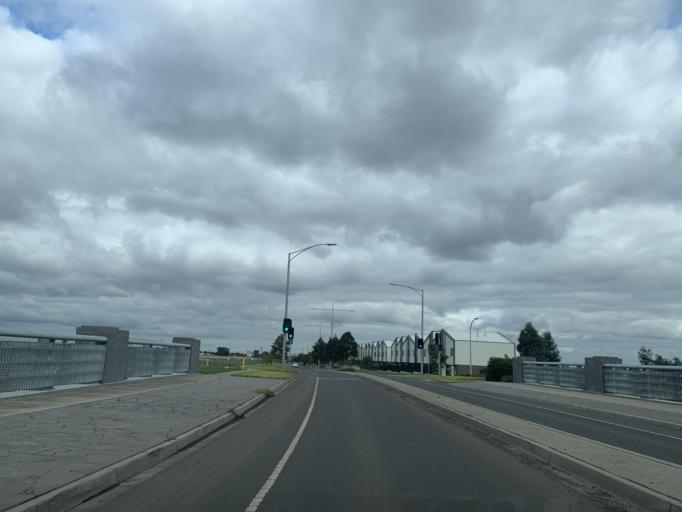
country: AU
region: Victoria
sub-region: Whittlesea
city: Epping
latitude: -37.6147
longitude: 145.0053
